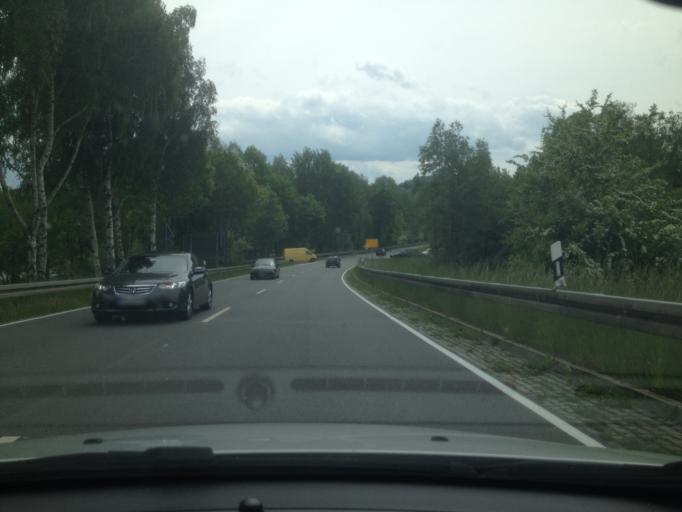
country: DE
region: Saxony
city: Stollberg
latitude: 50.6977
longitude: 12.7689
